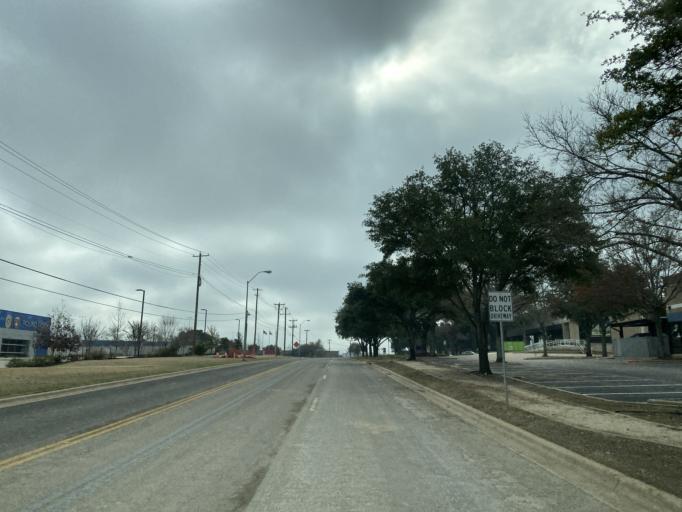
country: US
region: Texas
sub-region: Williamson County
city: Round Rock
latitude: 30.5423
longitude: -97.6892
